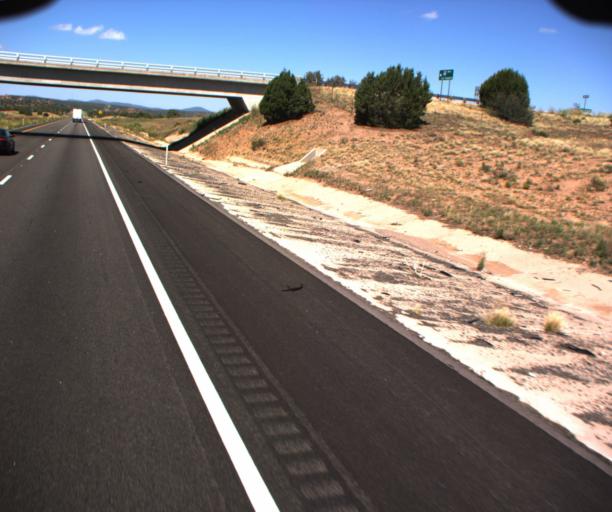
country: US
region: Arizona
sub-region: Mohave County
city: Peach Springs
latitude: 35.1909
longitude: -113.3646
